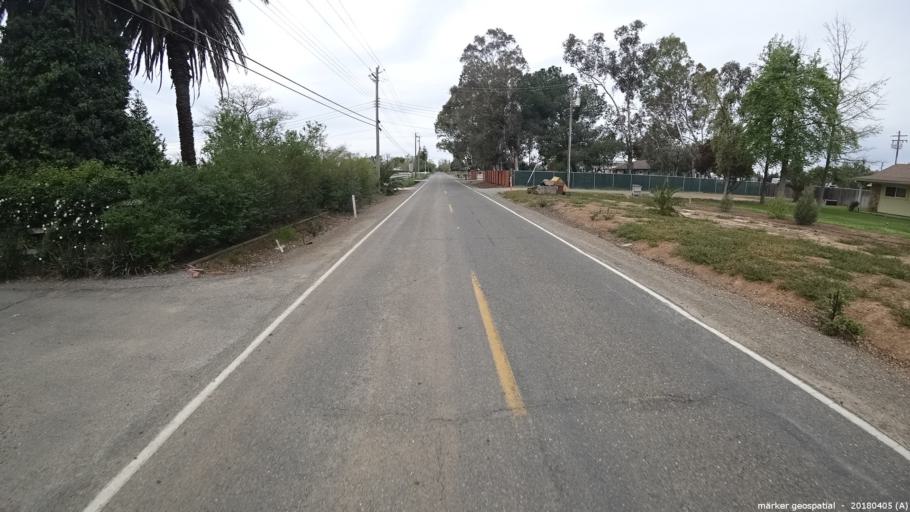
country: US
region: California
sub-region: Sacramento County
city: Galt
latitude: 38.2473
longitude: -121.3281
